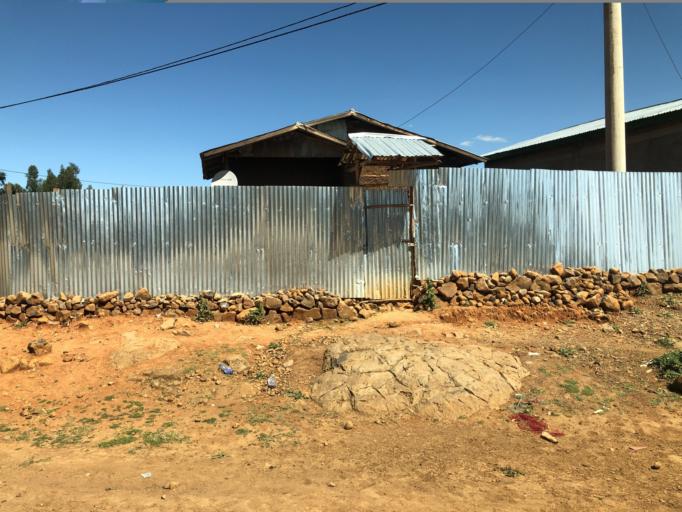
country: ET
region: Amhara
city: Lalibela
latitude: 11.6900
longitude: 38.9224
